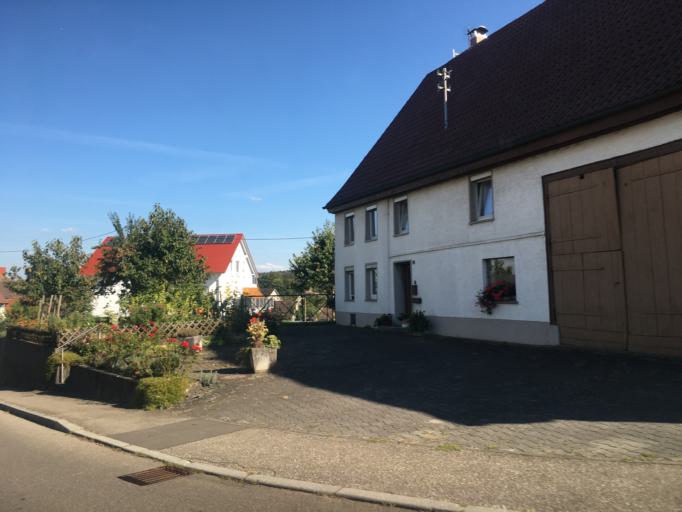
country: DE
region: Baden-Wuerttemberg
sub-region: Tuebingen Region
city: Obermarchtal
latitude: 48.2328
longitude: 9.5688
